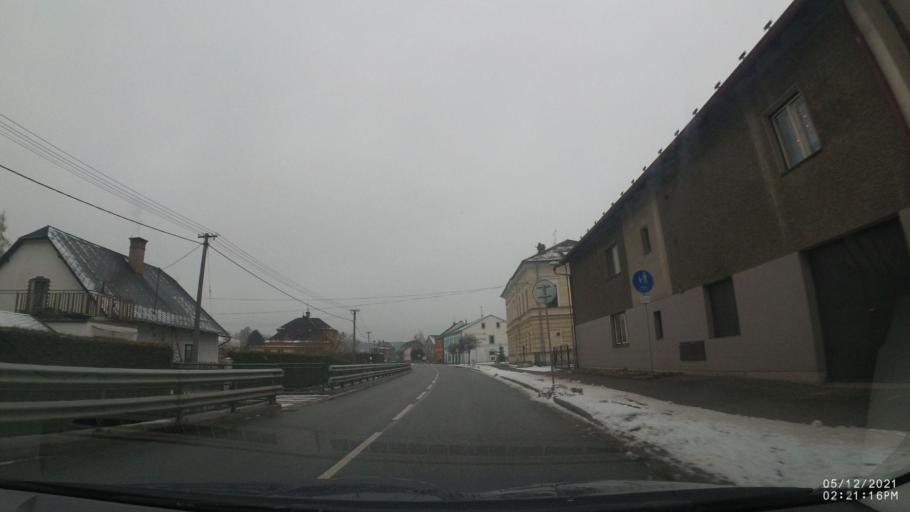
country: CZ
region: Kralovehradecky
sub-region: Okres Nachod
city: Nachod
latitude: 50.4390
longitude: 16.1511
